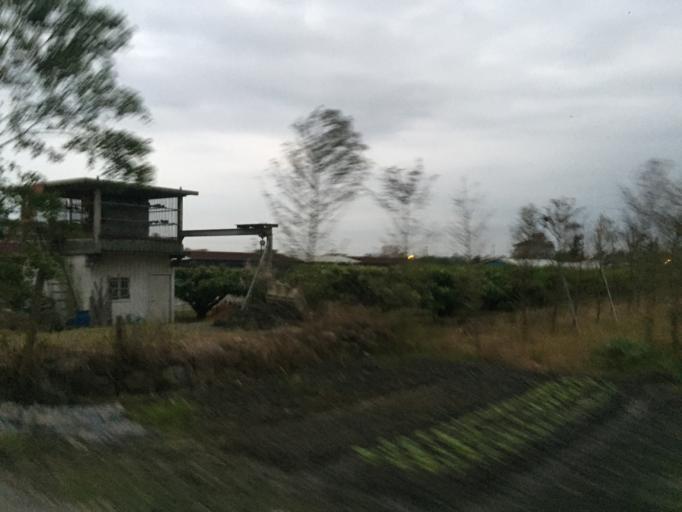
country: TW
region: Taiwan
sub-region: Yilan
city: Yilan
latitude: 24.7649
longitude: 121.7379
